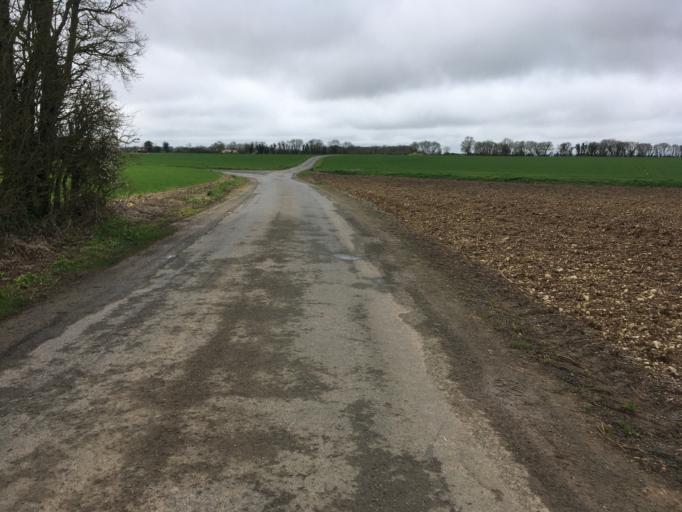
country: FR
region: Poitou-Charentes
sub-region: Departement de la Charente-Maritime
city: Saint-Germain-de-Marencennes
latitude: 46.1160
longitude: -0.8240
